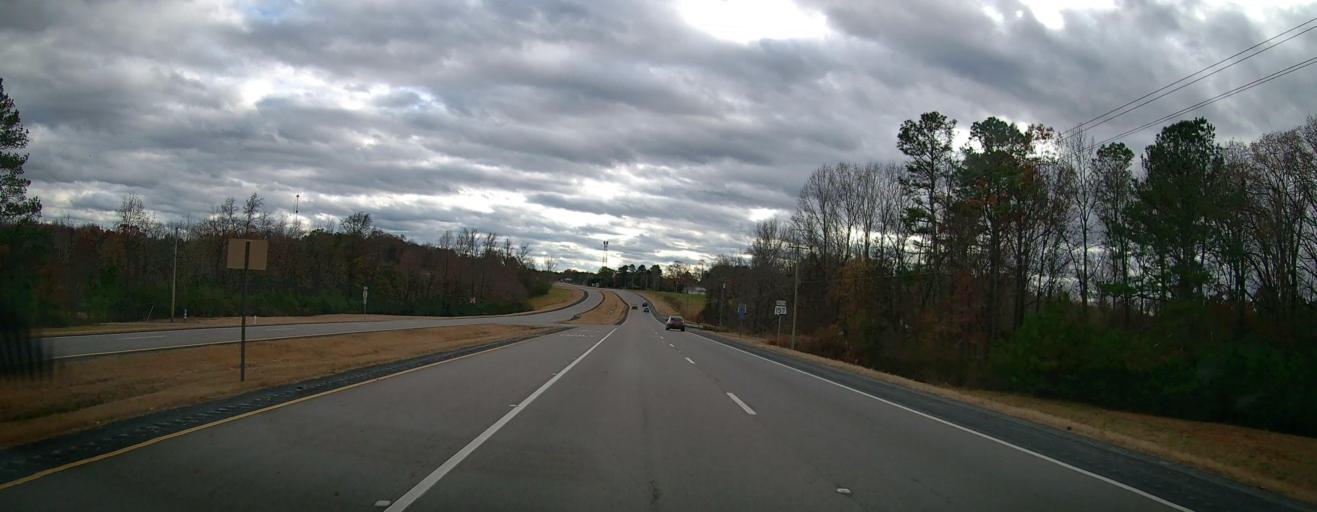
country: US
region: Alabama
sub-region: Morgan County
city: Falkville
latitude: 34.2979
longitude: -86.9978
